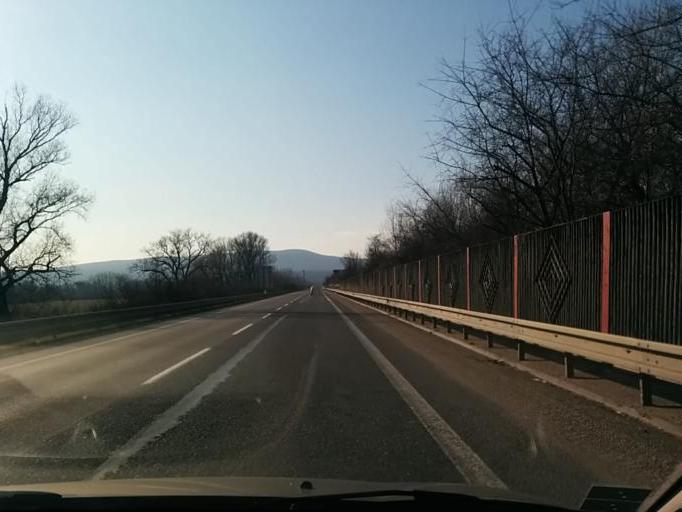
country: SK
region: Trenciansky
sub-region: Okres Nove Mesto nad Vahom
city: Nove Mesto nad Vahom
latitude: 48.7626
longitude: 17.8623
